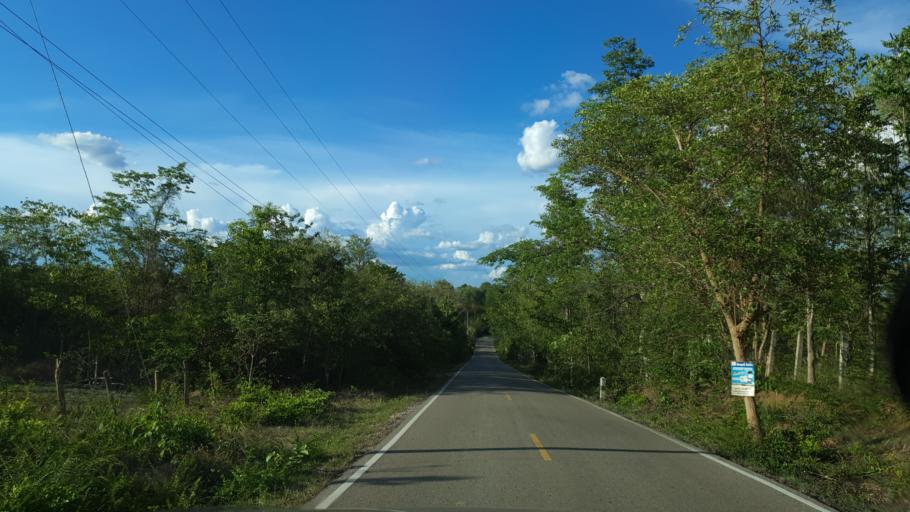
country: TH
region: Lampang
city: Sop Prap
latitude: 17.8786
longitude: 99.3096
